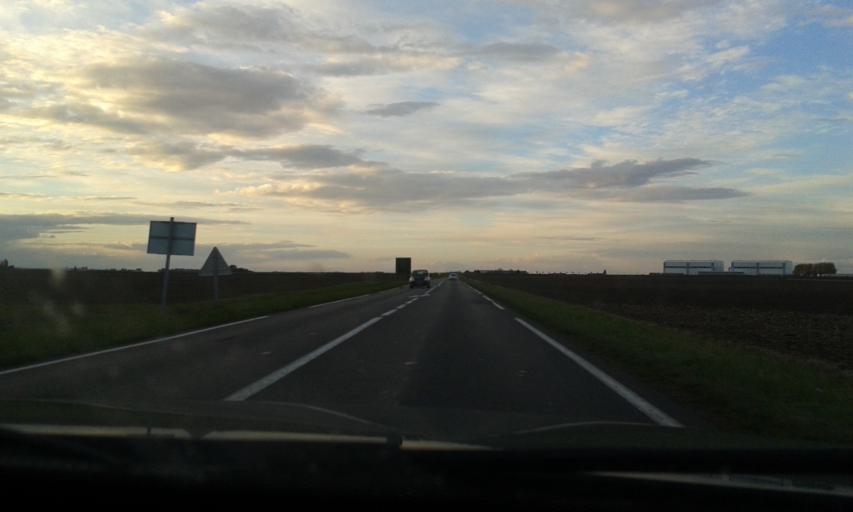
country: FR
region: Centre
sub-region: Departement du Loiret
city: Bricy
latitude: 47.9706
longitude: 1.7750
